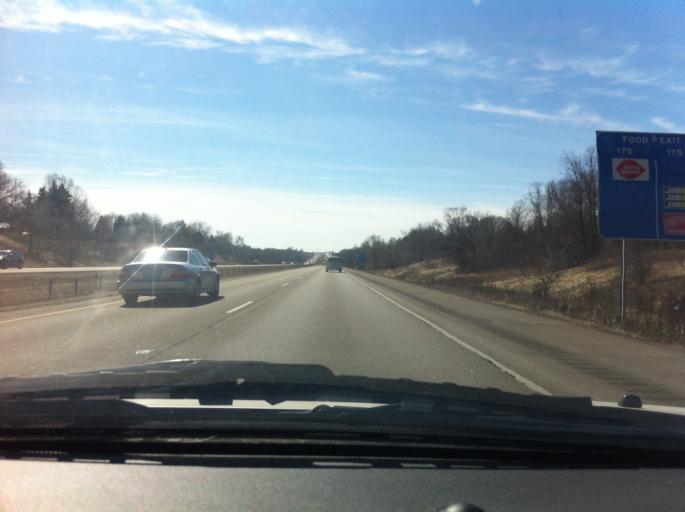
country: US
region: Wisconsin
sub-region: Rock County
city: Janesville
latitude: 42.7387
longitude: -89.0053
